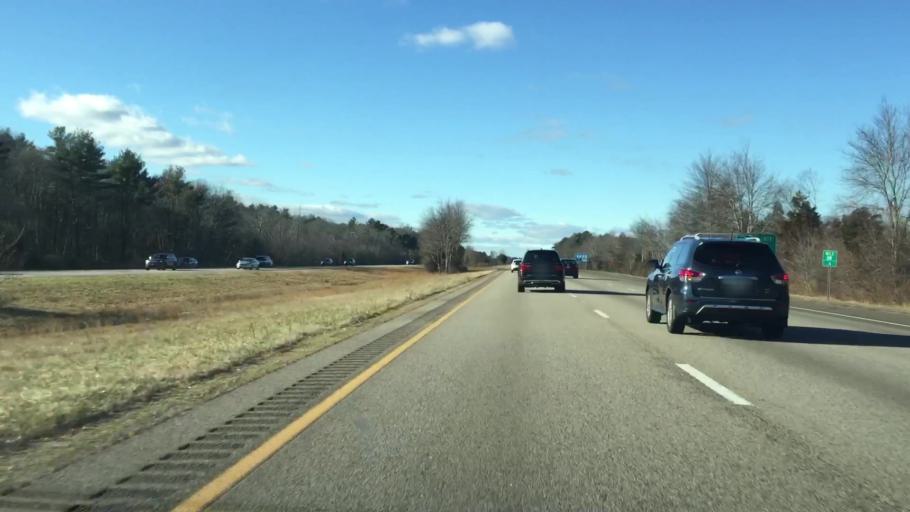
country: US
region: Massachusetts
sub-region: Bristol County
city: Norton Center
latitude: 41.9949
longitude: -71.1866
